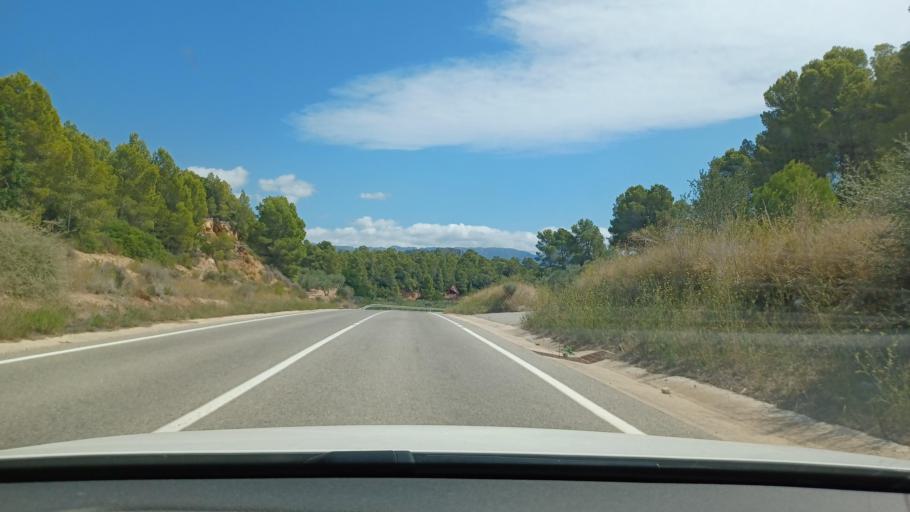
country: ES
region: Catalonia
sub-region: Provincia de Tarragona
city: Tivenys
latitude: 40.9411
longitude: 0.4638
